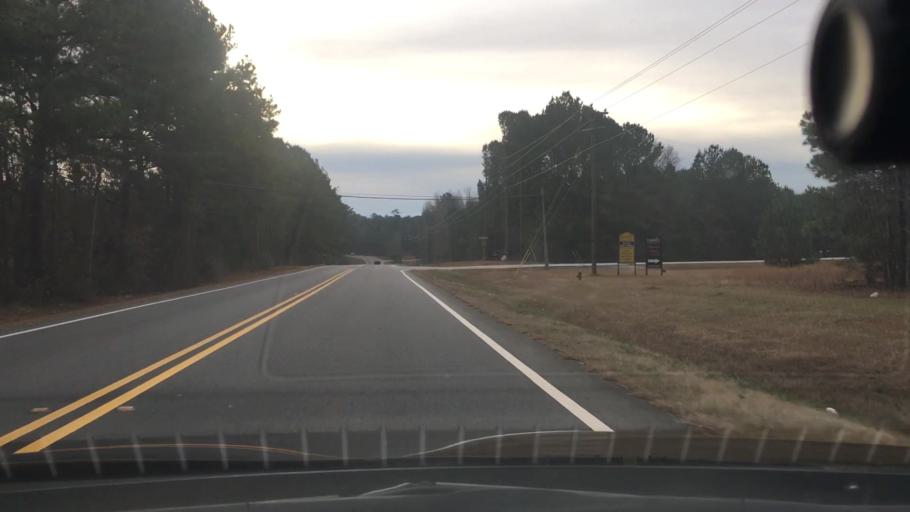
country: US
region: Georgia
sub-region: Coweta County
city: Senoia
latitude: 33.2662
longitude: -84.5218
